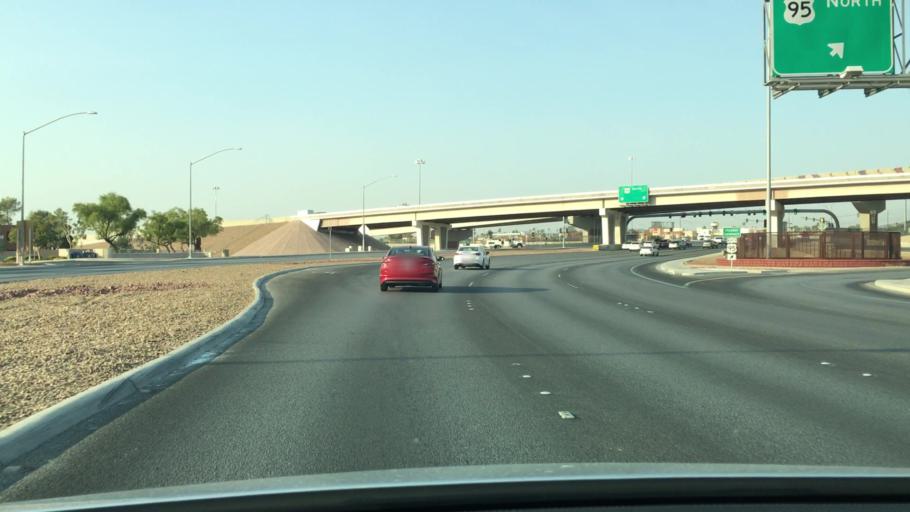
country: US
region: Nevada
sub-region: Clark County
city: Spring Valley
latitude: 36.1785
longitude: -115.2425
